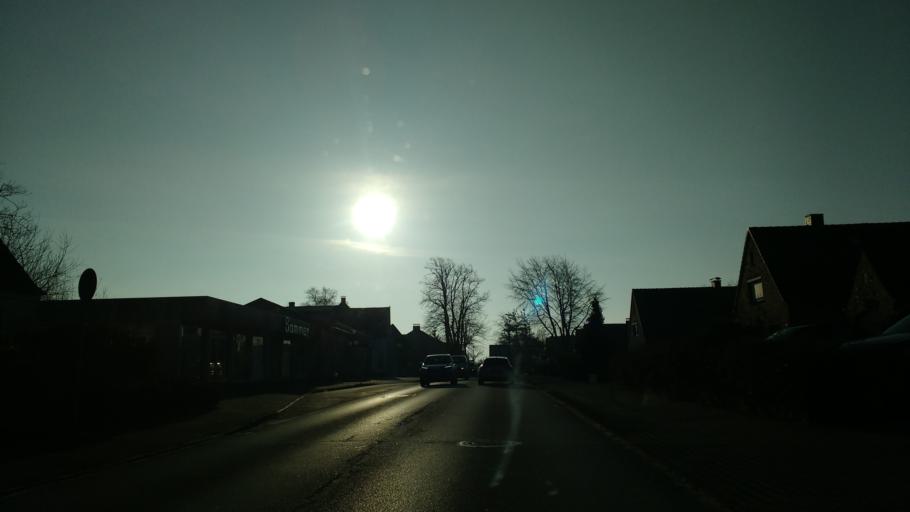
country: DE
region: Schleswig-Holstein
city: Schenefeld
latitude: 54.0427
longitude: 9.4807
